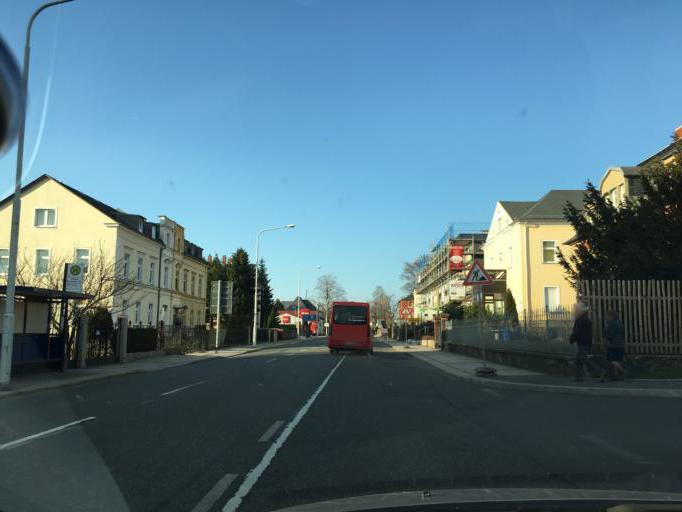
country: DE
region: Saxony
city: Limbach-Oberfrohna
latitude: 50.8593
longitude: 12.7678
